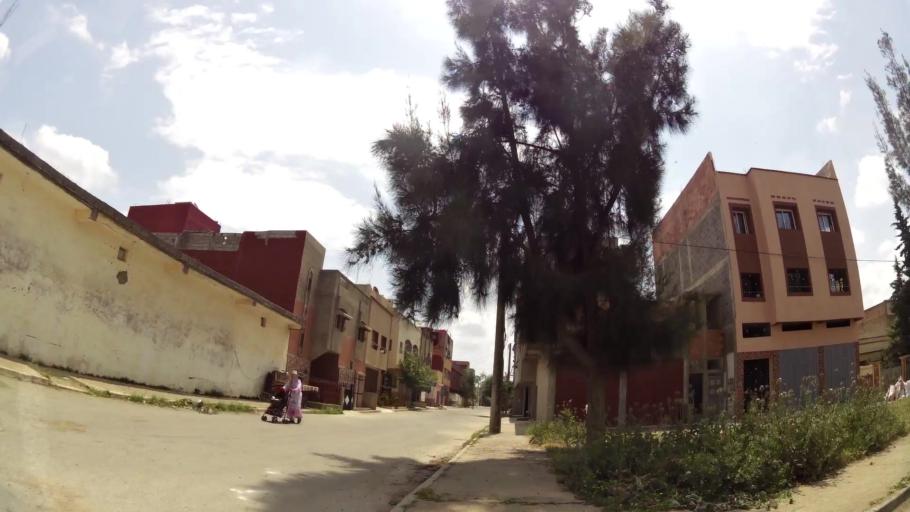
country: MA
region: Rabat-Sale-Zemmour-Zaer
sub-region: Khemisset
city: Tiflet
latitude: 34.0031
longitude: -6.5331
